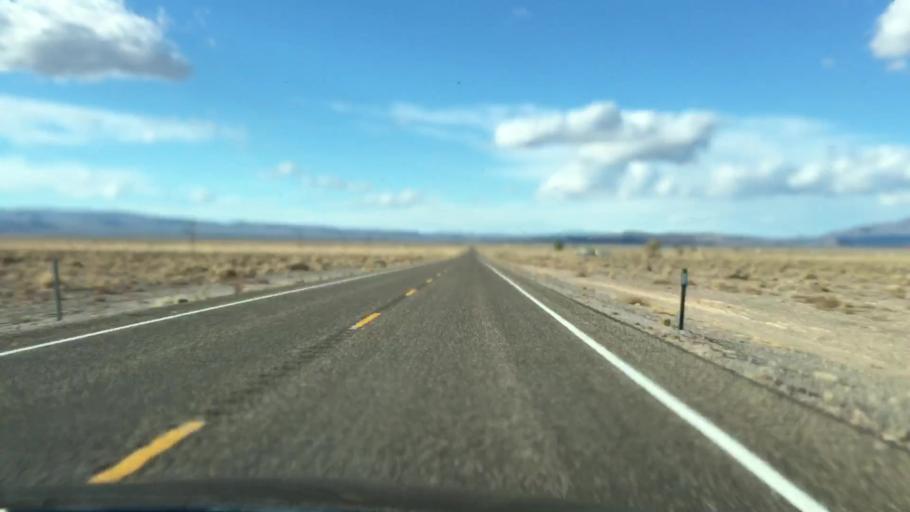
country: US
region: Nevada
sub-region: Nye County
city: Beatty
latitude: 37.2463
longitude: -117.0000
